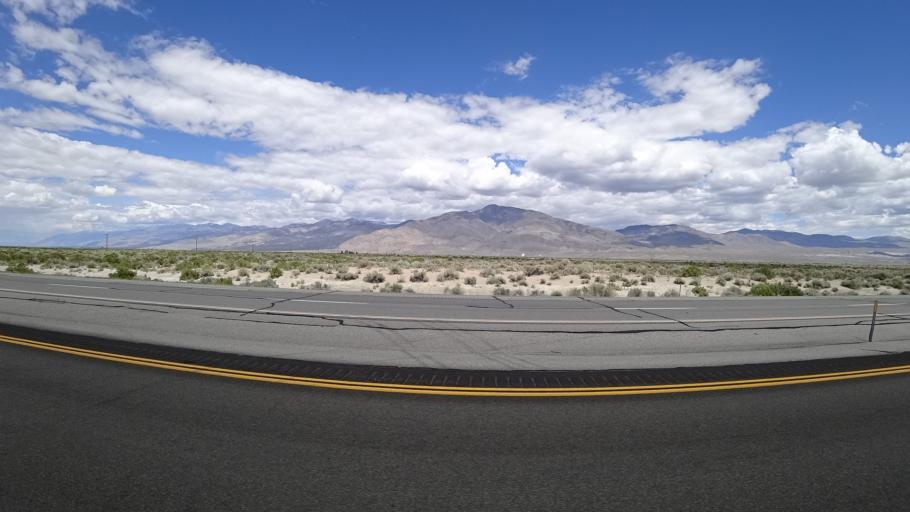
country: US
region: California
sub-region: Inyo County
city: Big Pine
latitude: 37.2112
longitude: -118.3277
